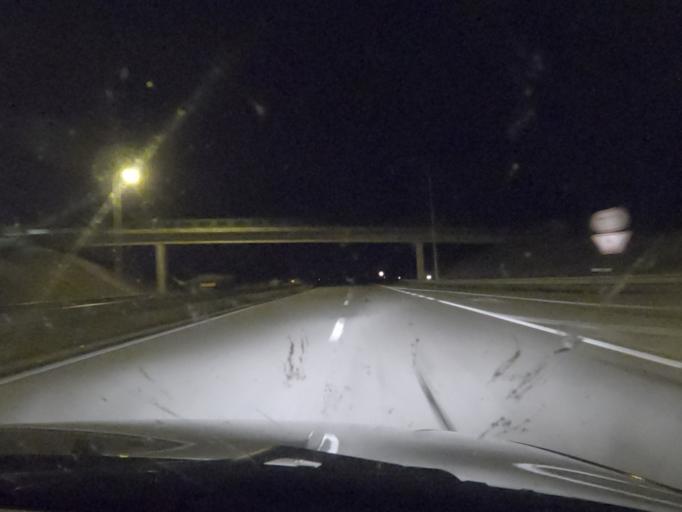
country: PT
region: Evora
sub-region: Estremoz
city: Estremoz
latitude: 38.8247
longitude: -7.6091
